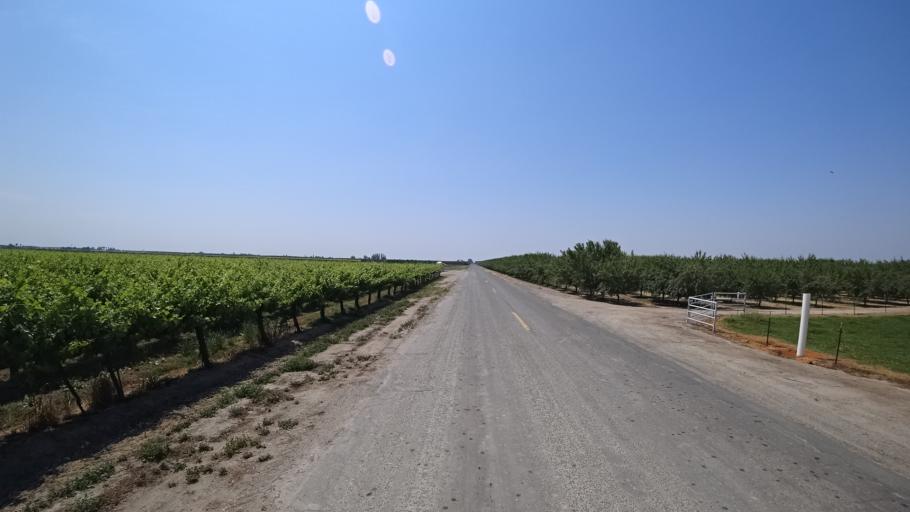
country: US
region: California
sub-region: Kings County
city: Lemoore
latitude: 36.3535
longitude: -119.7629
